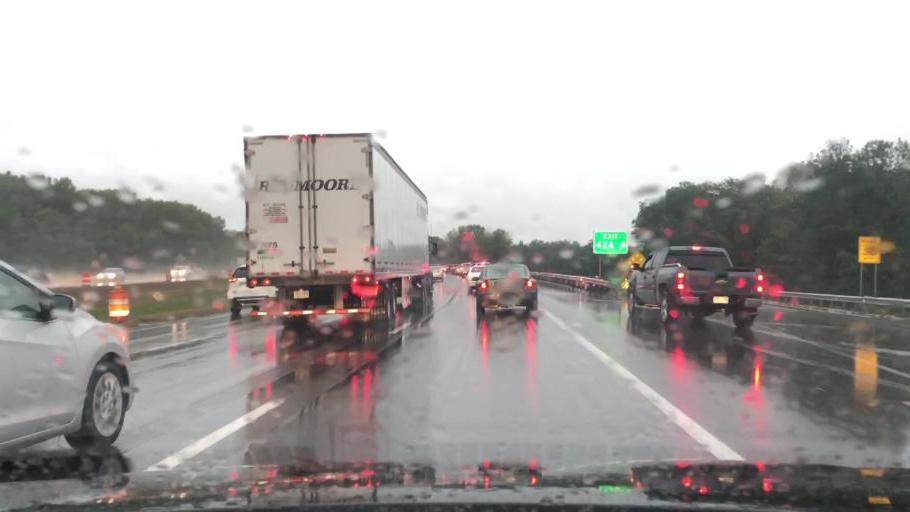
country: US
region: Massachusetts
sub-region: Essex County
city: North Andover
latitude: 42.6834
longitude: -71.1446
